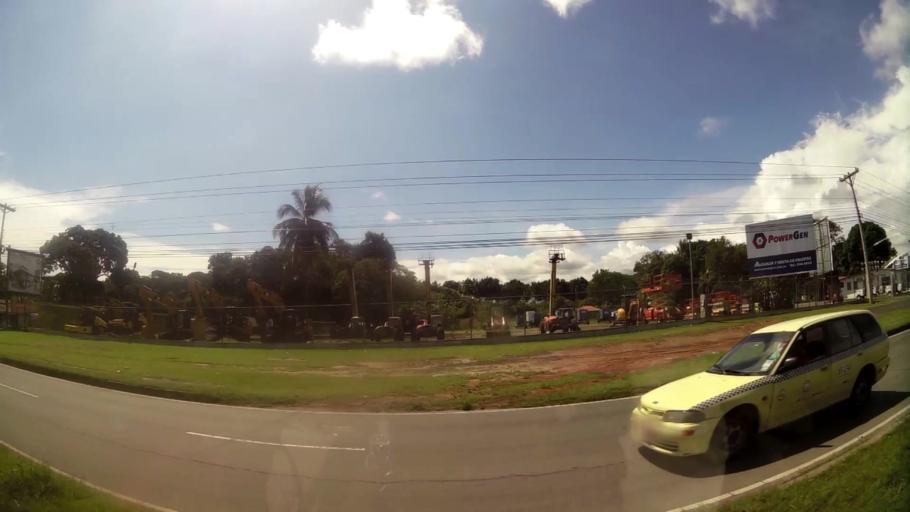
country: PA
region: Panama
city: Chame
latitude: 8.5856
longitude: -79.8845
